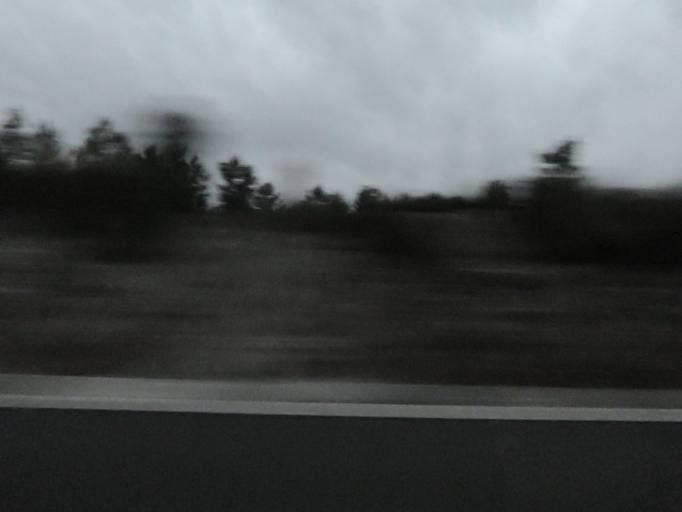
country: PT
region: Setubal
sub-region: Seixal
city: Arrentela
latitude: 38.5954
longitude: -9.1007
